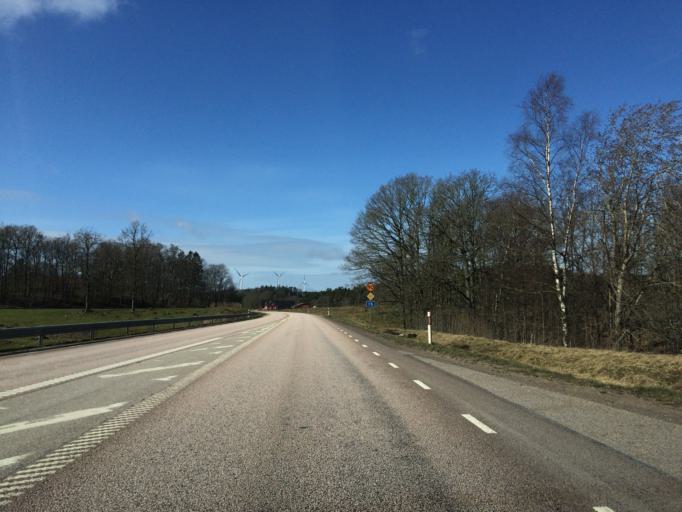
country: SE
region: Halland
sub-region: Laholms Kommun
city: Knared
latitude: 56.5257
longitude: 13.2462
